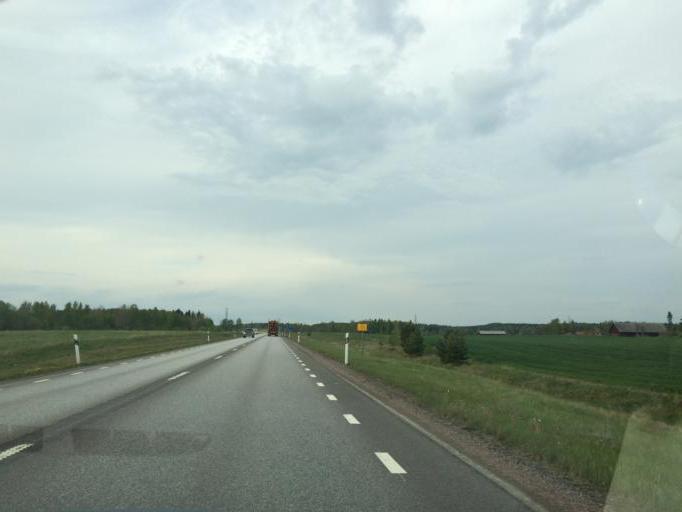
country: SE
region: Vaestmanland
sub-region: Kopings Kommun
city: Koping
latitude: 59.5307
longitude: 15.9578
